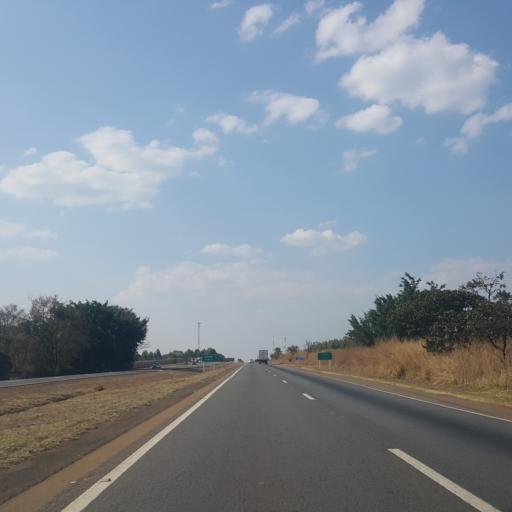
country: BR
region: Goias
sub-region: Abadiania
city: Abadiania
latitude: -16.2287
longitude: -48.7542
